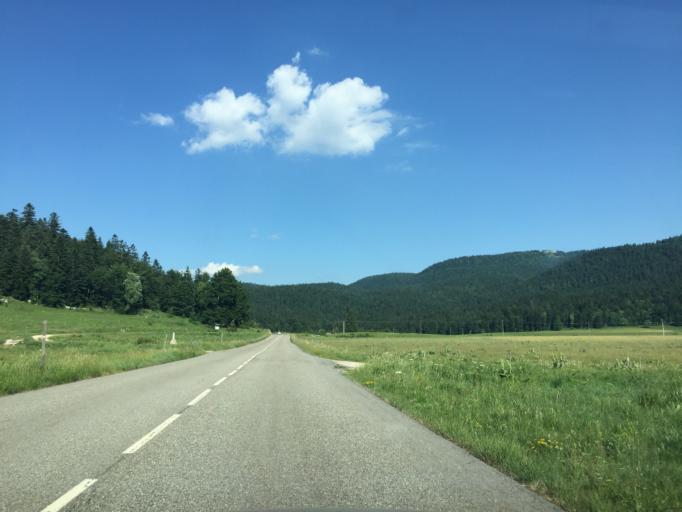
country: FR
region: Rhone-Alpes
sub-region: Departement de la Drome
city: Saint-Jean-en-Royans
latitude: 44.9465
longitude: 5.3138
